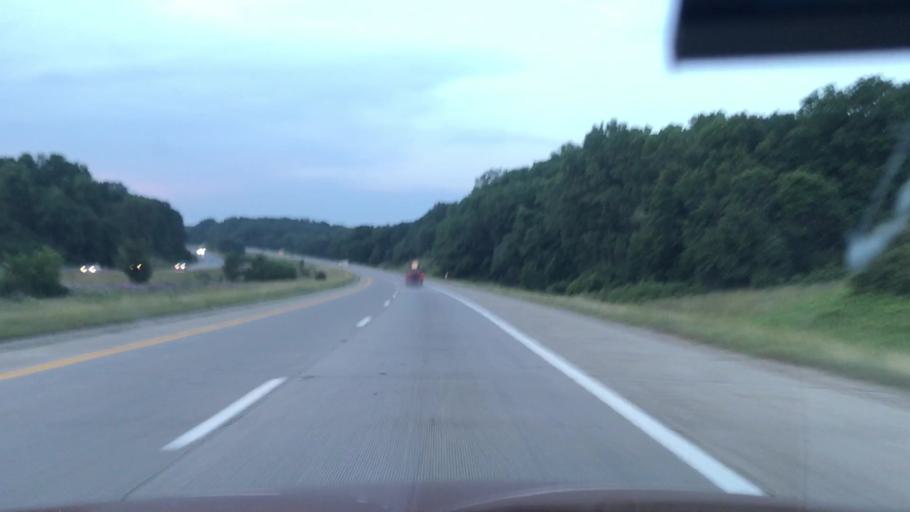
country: US
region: Michigan
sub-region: Kent County
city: Comstock Park
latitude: 43.0732
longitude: -85.6450
